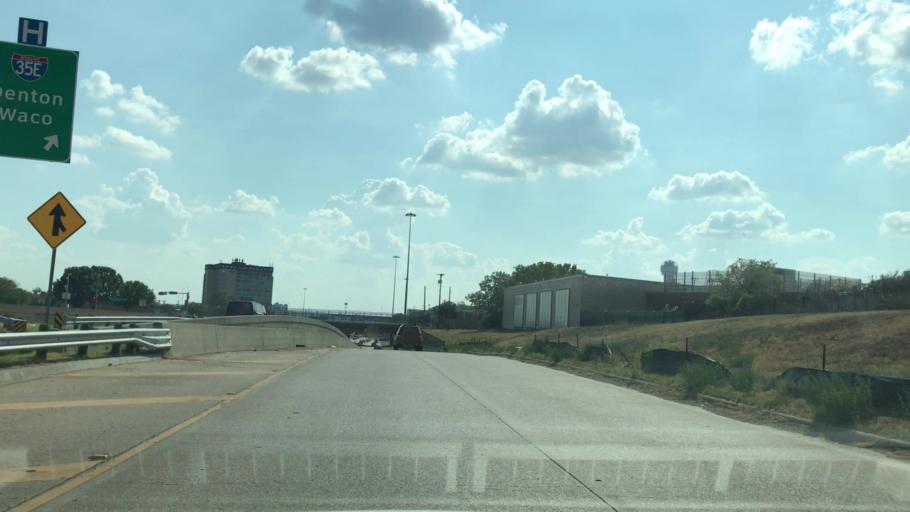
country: US
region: Texas
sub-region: Dallas County
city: Dallas
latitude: 32.7754
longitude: -96.7897
